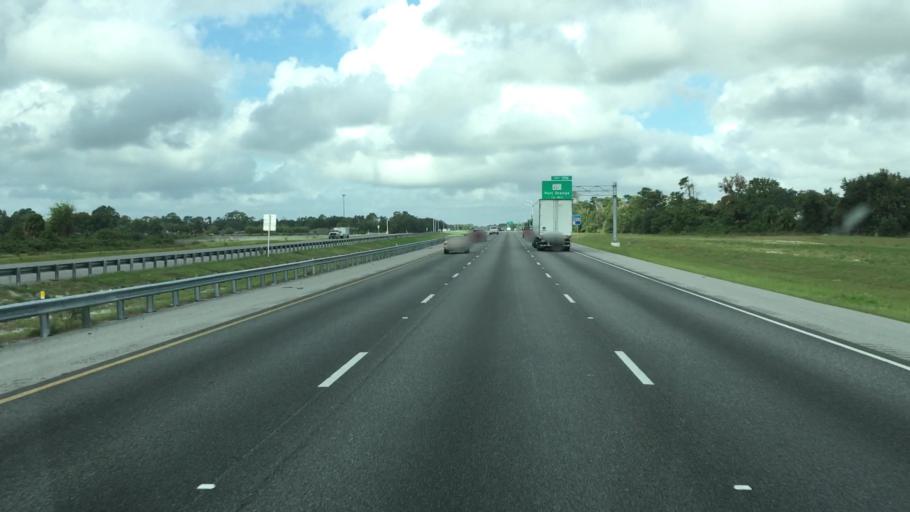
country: US
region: Florida
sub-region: Volusia County
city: Port Orange
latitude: 29.0936
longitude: -81.0223
